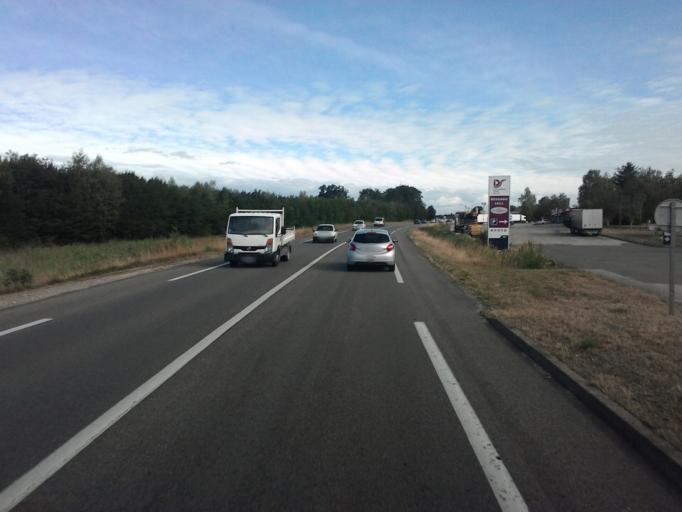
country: FR
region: Rhone-Alpes
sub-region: Departement de l'Ain
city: Montagnat
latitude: 46.1684
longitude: 5.2624
